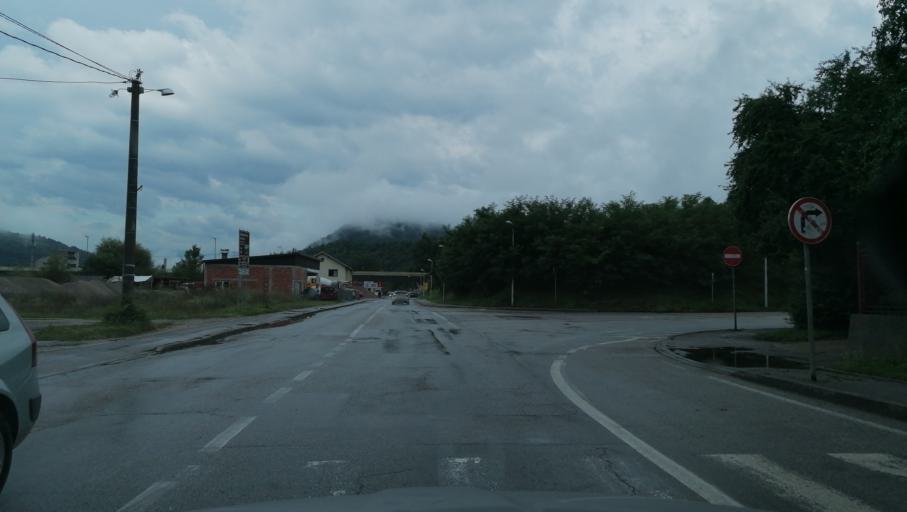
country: BA
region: Republika Srpska
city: Visegrad
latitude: 43.7889
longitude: 19.2958
